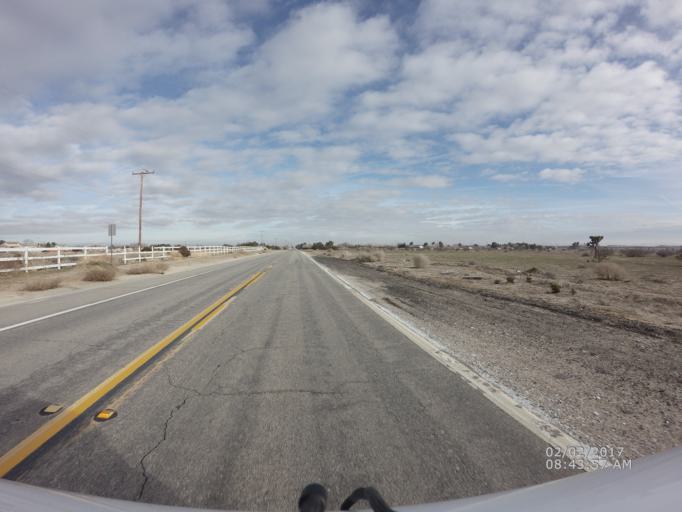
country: US
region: California
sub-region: Los Angeles County
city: Littlerock
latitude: 34.5325
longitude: -118.0277
